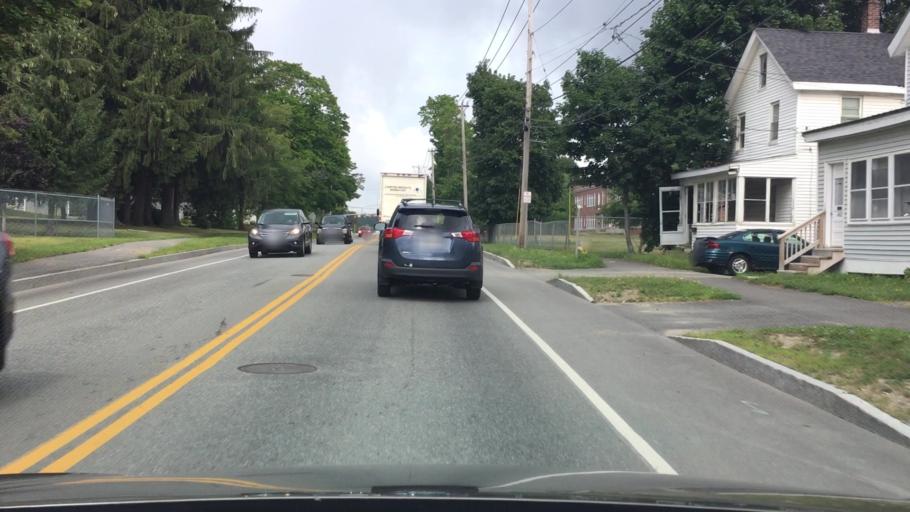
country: US
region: Maine
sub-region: Penobscot County
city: Bangor
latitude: 44.8159
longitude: -68.7722
